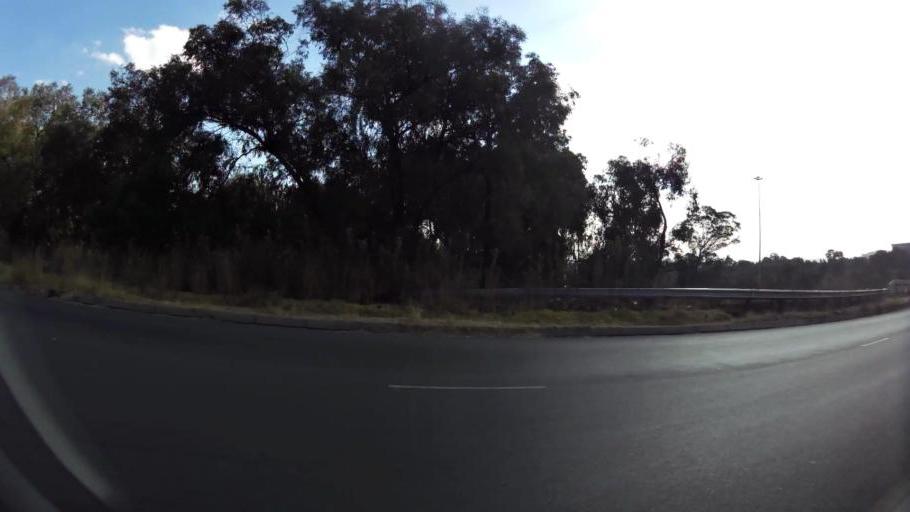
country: ZA
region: Gauteng
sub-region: City of Johannesburg Metropolitan Municipality
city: Johannesburg
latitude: -26.2629
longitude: 27.9728
